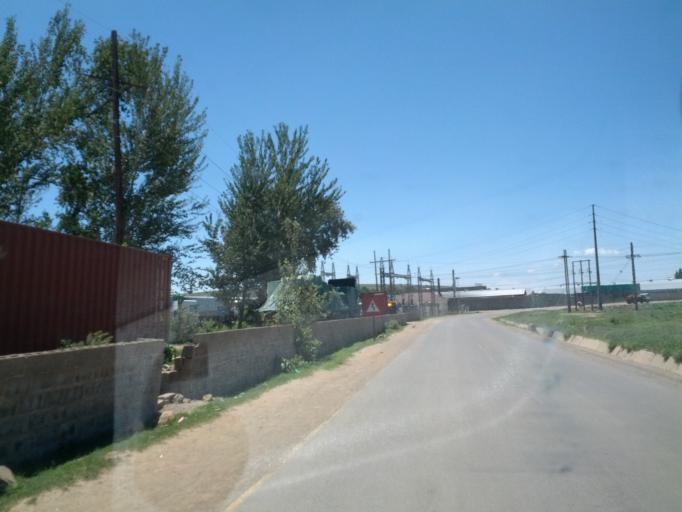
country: LS
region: Maseru
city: Maseru
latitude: -29.2967
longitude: 27.4637
